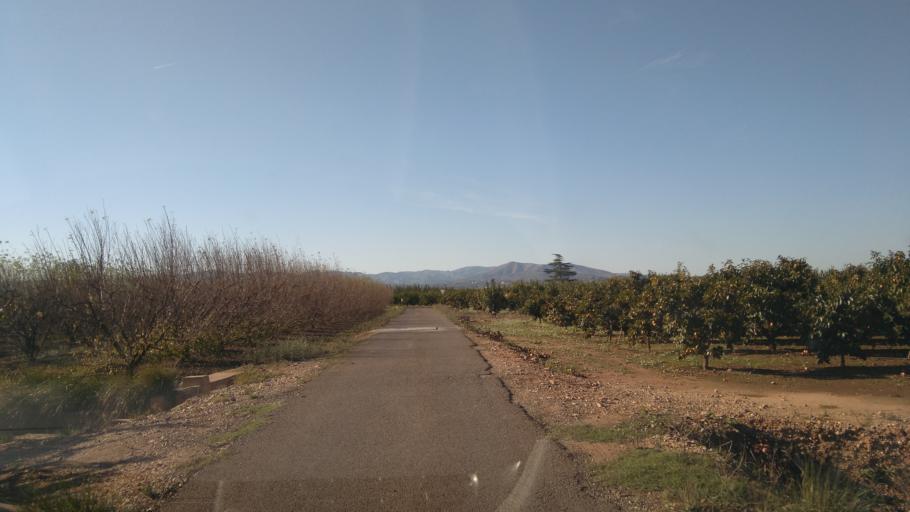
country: ES
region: Valencia
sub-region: Provincia de Valencia
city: L'Alcudia
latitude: 39.1857
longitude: -0.5226
